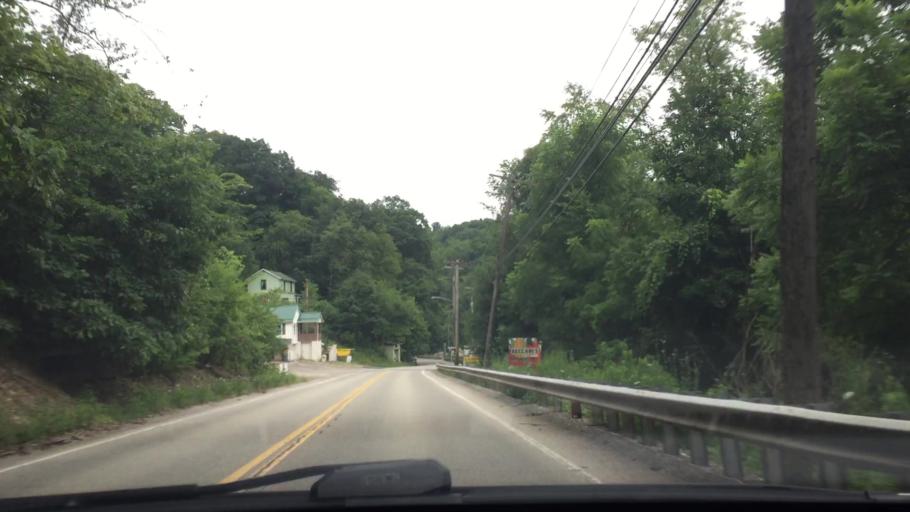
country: US
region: Pennsylvania
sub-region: Allegheny County
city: Rennerdale
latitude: 40.3744
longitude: -80.1341
